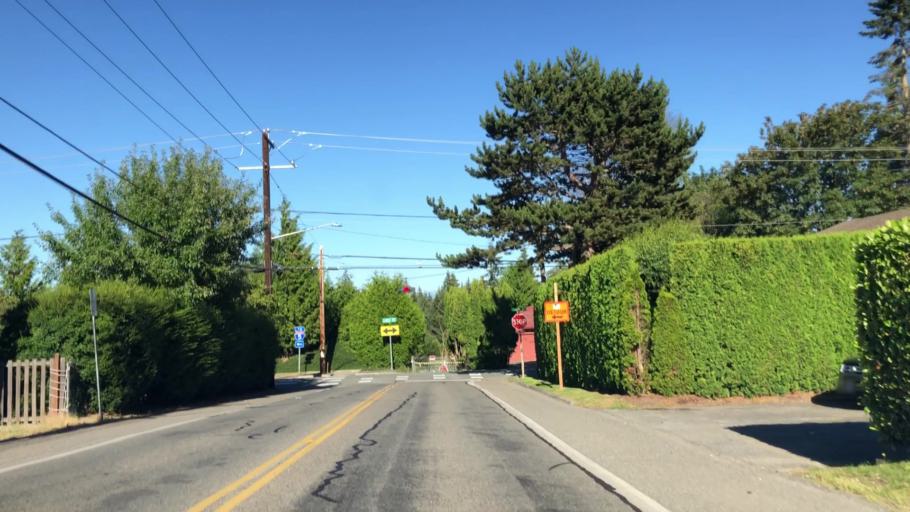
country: US
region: Washington
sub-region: Snohomish County
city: Martha Lake
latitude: 47.8369
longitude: -122.2469
